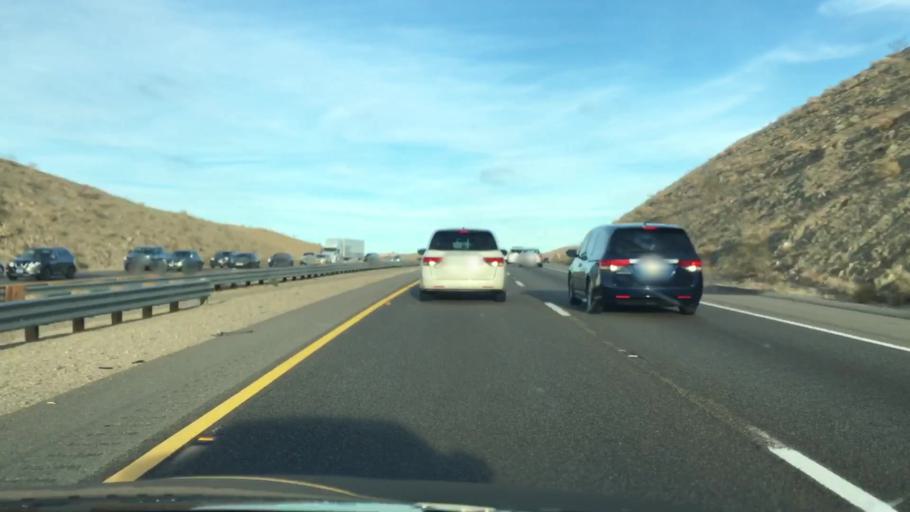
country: US
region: California
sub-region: San Bernardino County
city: Barstow
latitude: 34.9047
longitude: -116.9822
